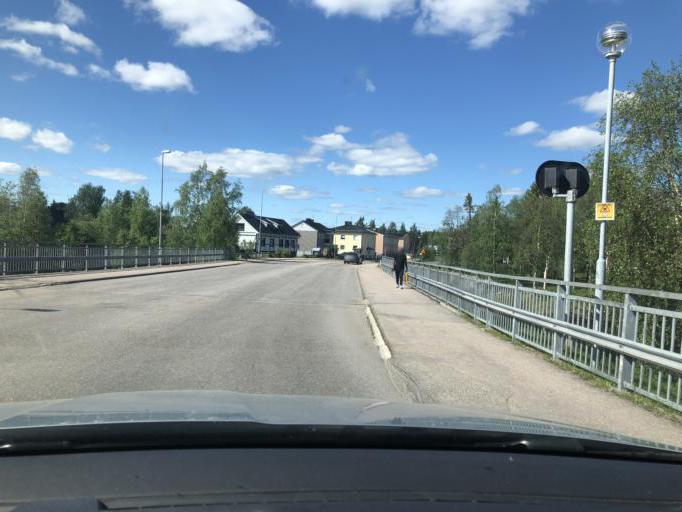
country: SE
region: Norrbotten
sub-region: Gallivare Kommun
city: Gaellivare
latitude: 67.1317
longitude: 20.6830
